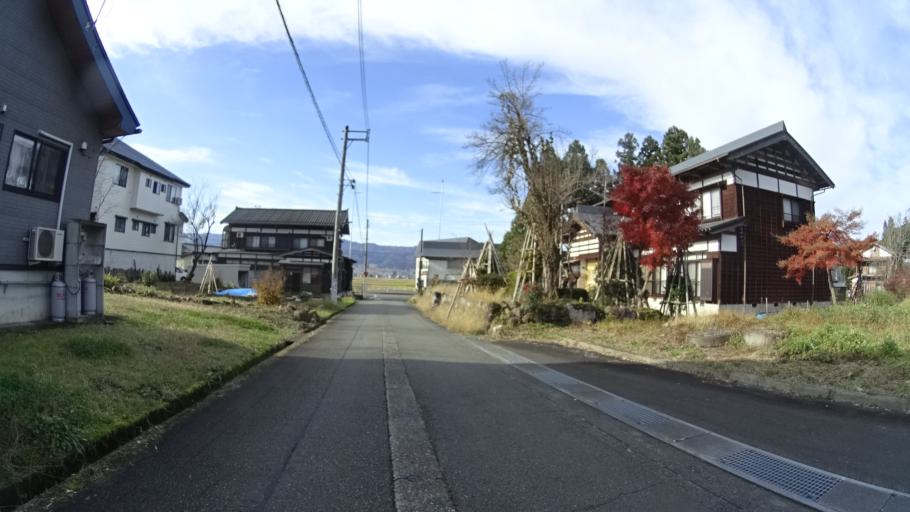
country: JP
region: Niigata
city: Muikamachi
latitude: 37.0325
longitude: 138.8880
